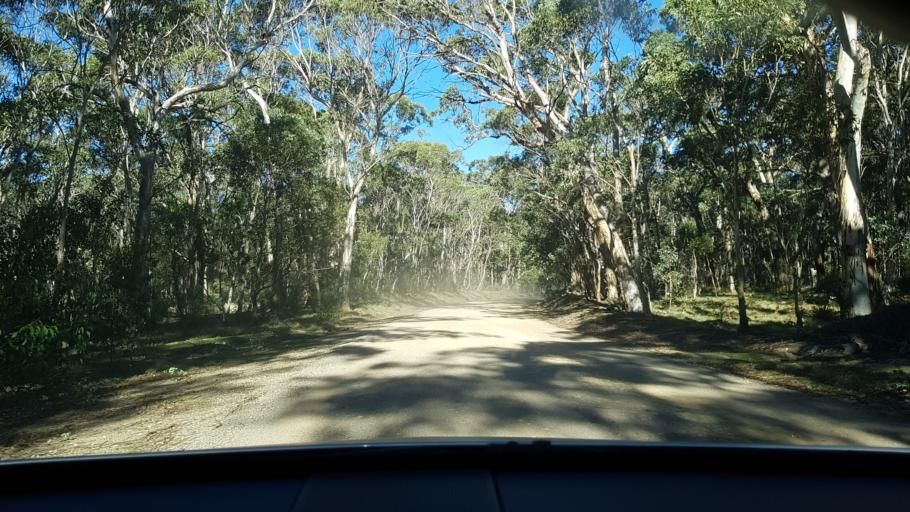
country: AU
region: New South Wales
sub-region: Oberon
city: Oberon
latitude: -33.9266
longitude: 150.0553
